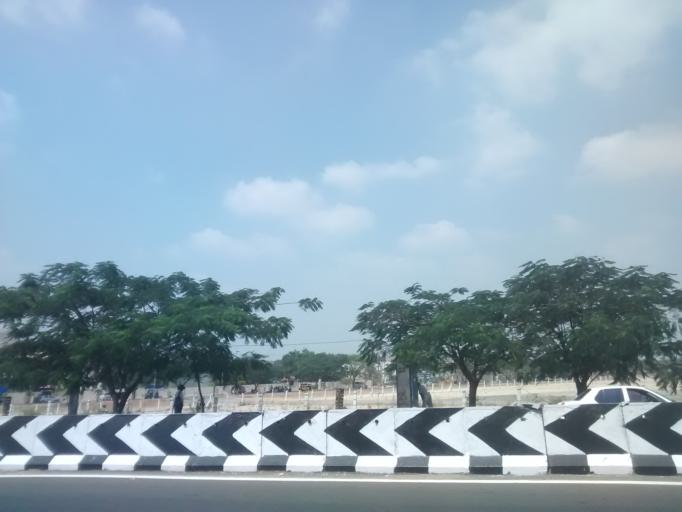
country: IN
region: Tamil Nadu
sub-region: Coimbatore
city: Singanallur
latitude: 11.0312
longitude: 77.0290
